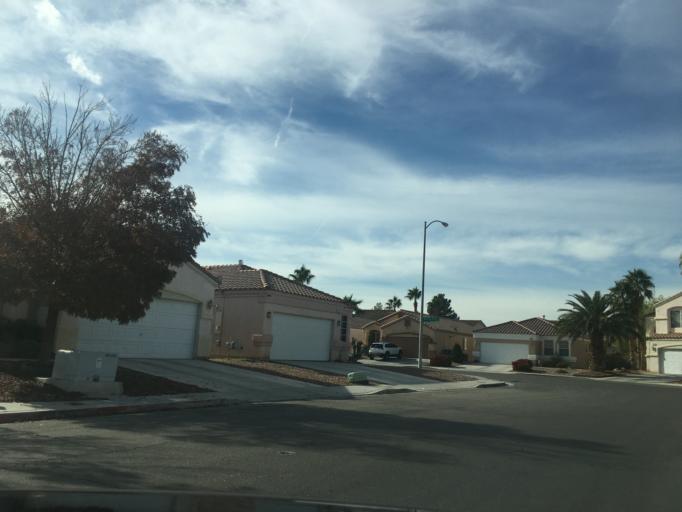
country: US
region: Nevada
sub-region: Clark County
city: Enterprise
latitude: 36.0168
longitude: -115.1679
